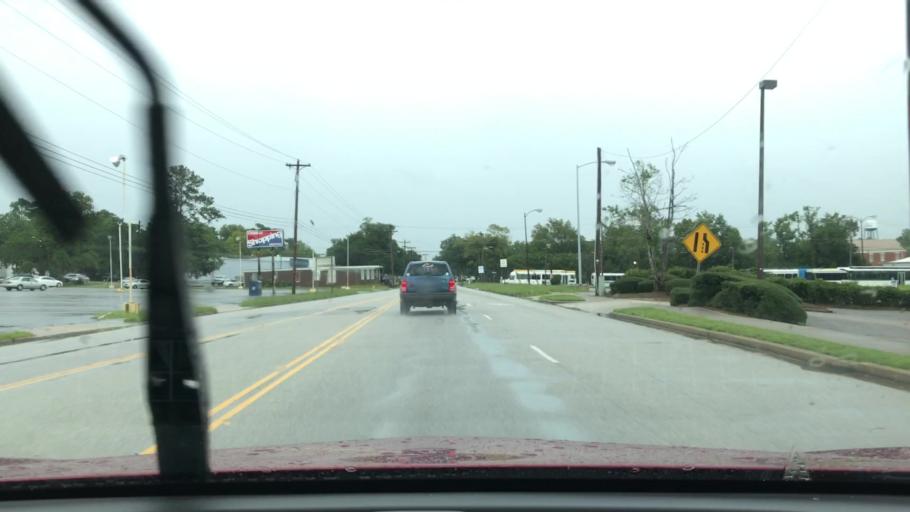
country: US
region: South Carolina
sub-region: Horry County
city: Conway
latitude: 33.8323
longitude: -79.0555
